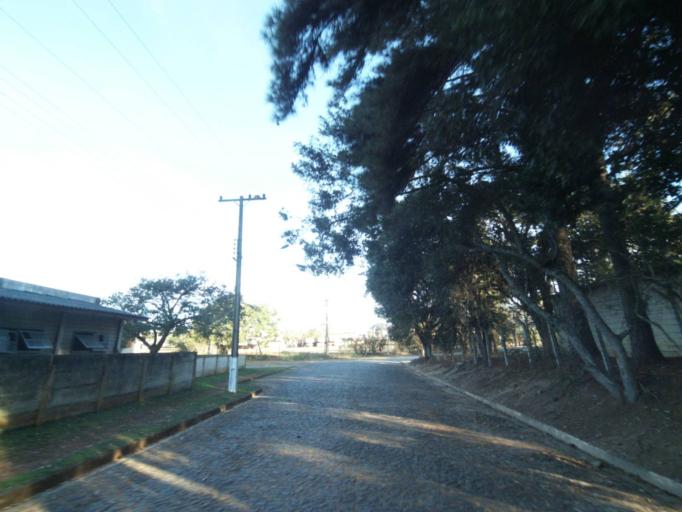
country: BR
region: Parana
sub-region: Tibagi
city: Tibagi
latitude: -24.5075
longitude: -50.4170
